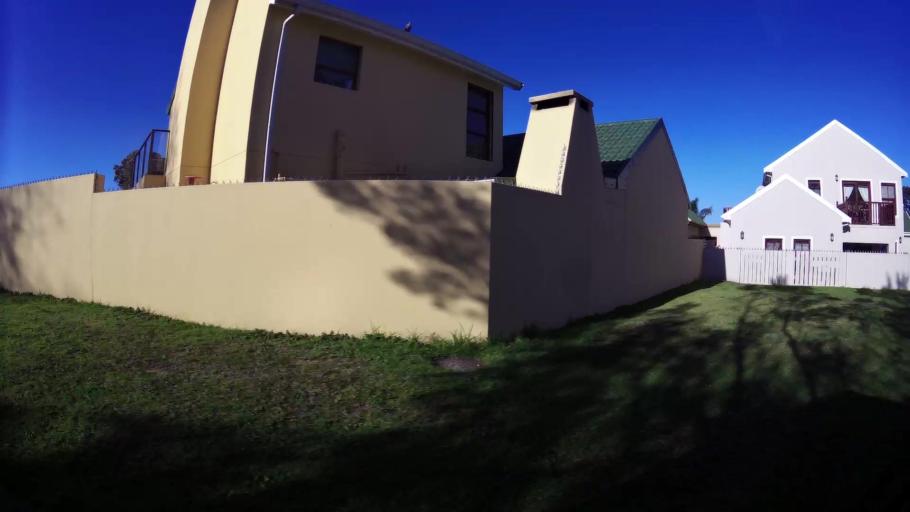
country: ZA
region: Western Cape
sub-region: Eden District Municipality
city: George
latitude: -33.9621
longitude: 22.4438
